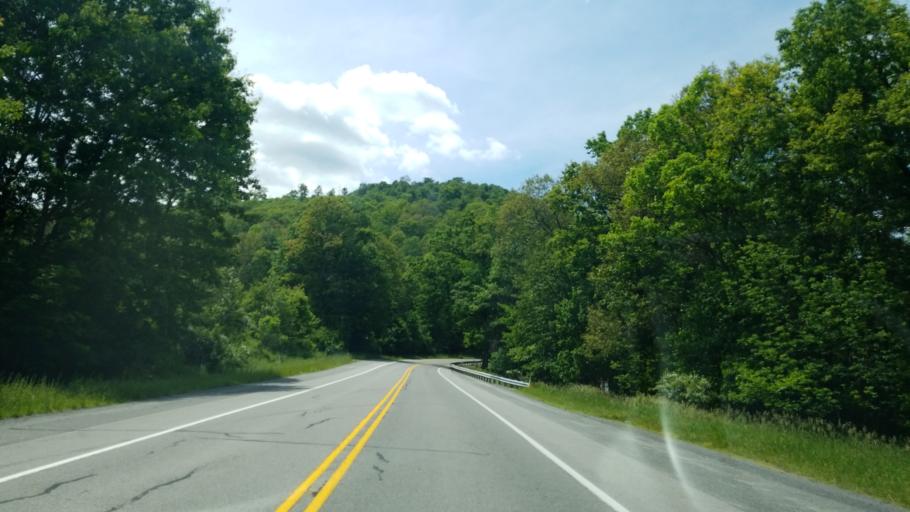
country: US
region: Pennsylvania
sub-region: Blair County
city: Tyrone
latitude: 40.6933
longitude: -78.2781
